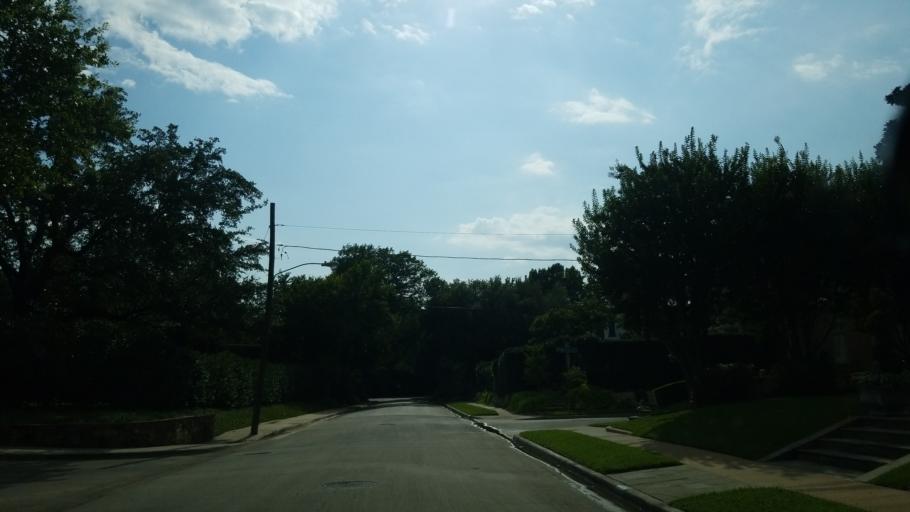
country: US
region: Texas
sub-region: Dallas County
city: University Park
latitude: 32.8419
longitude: -96.8018
